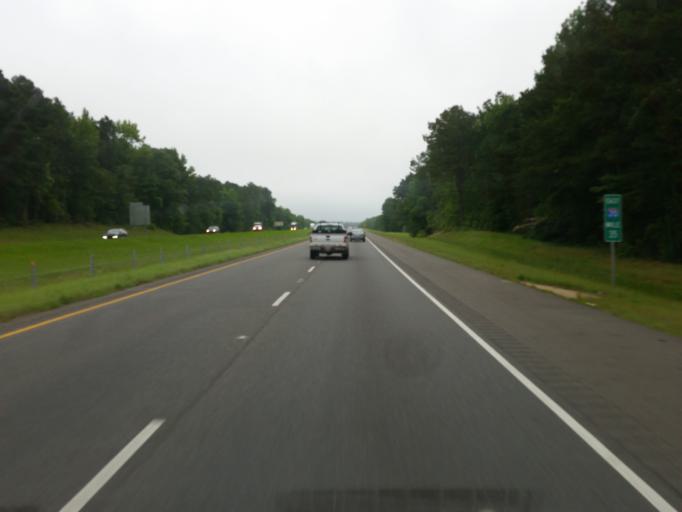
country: US
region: Louisiana
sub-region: Bossier Parish
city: Haughton
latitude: 32.5612
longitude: -93.4990
